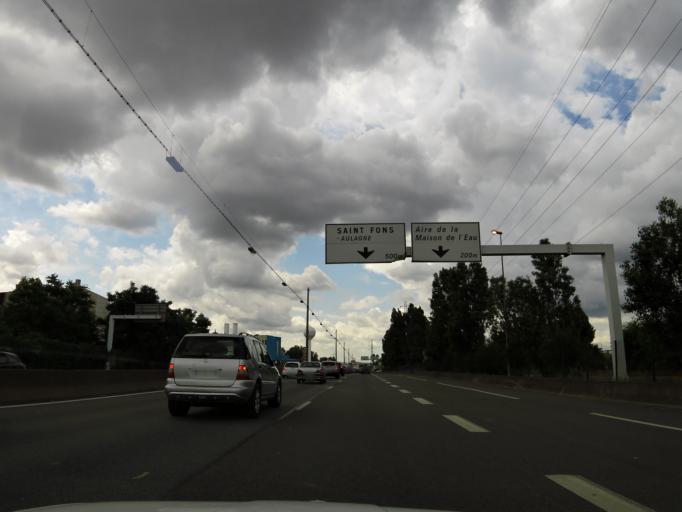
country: FR
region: Rhone-Alpes
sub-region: Departement du Rhone
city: Saint-Fons
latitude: 45.7101
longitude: 4.8434
